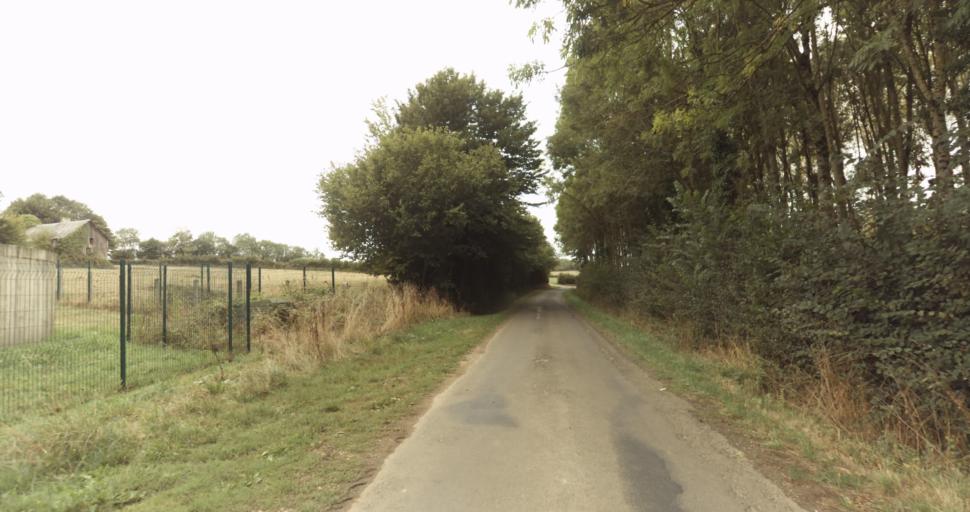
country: FR
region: Lower Normandy
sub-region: Departement de l'Orne
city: Gace
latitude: 48.8159
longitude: 0.3650
